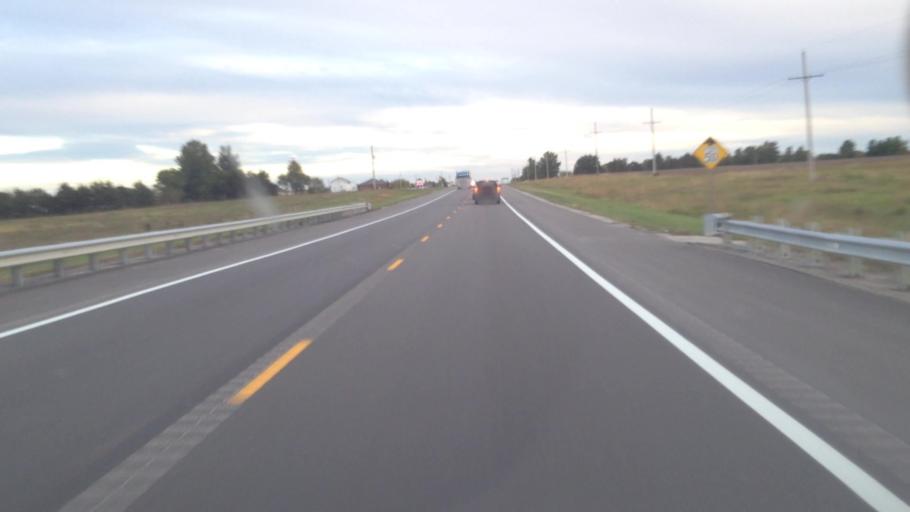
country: US
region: Kansas
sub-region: Franklin County
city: Ottawa
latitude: 38.4967
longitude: -95.2672
